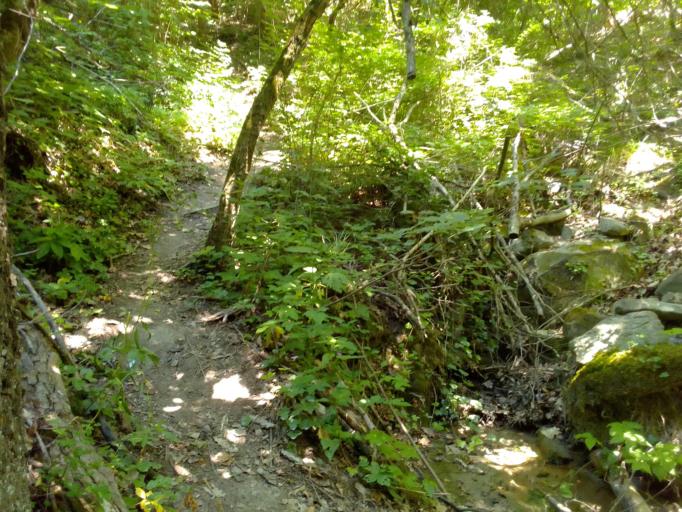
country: IT
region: Emilia-Romagna
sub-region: Provincia di Piacenza
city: Pianello Val Tidone
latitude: 44.9100
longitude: 9.4035
